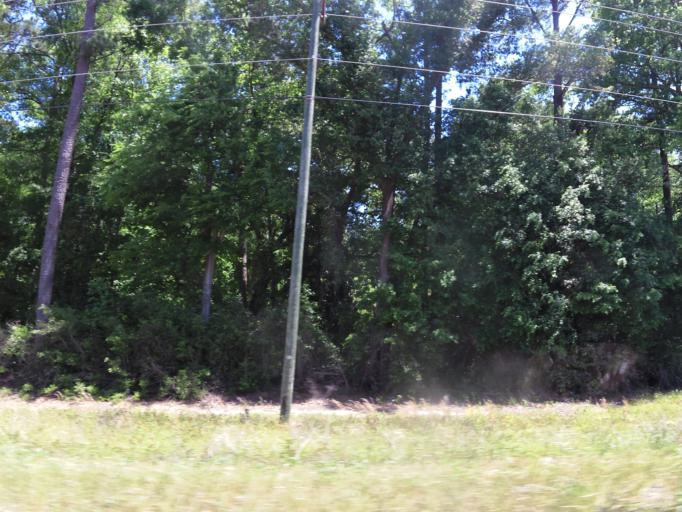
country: US
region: South Carolina
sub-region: Aiken County
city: Gloverville
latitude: 33.5371
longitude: -81.8340
